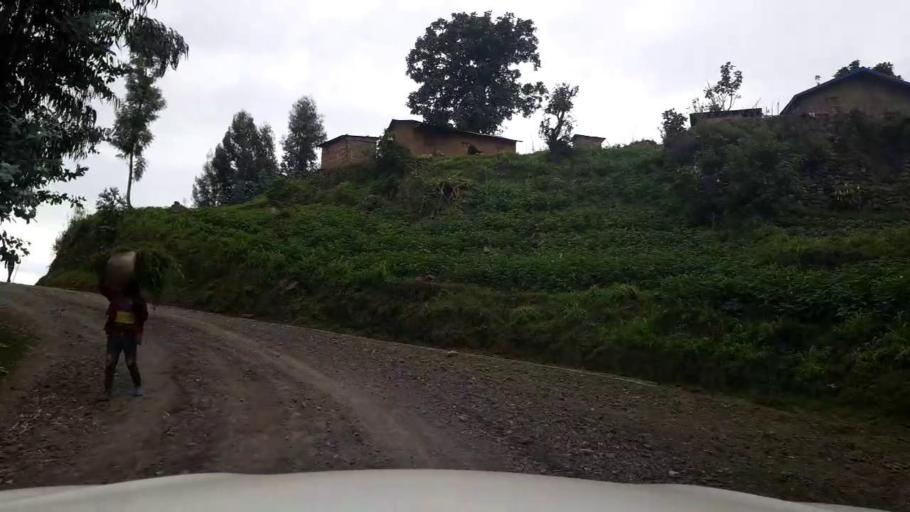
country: RW
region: Northern Province
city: Musanze
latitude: -1.5128
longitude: 29.5345
